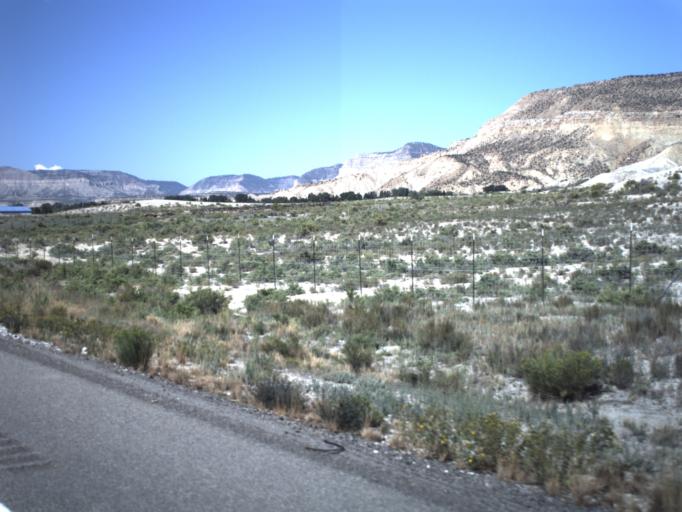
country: US
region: Utah
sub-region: Emery County
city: Ferron
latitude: 38.9309
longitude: -111.2334
